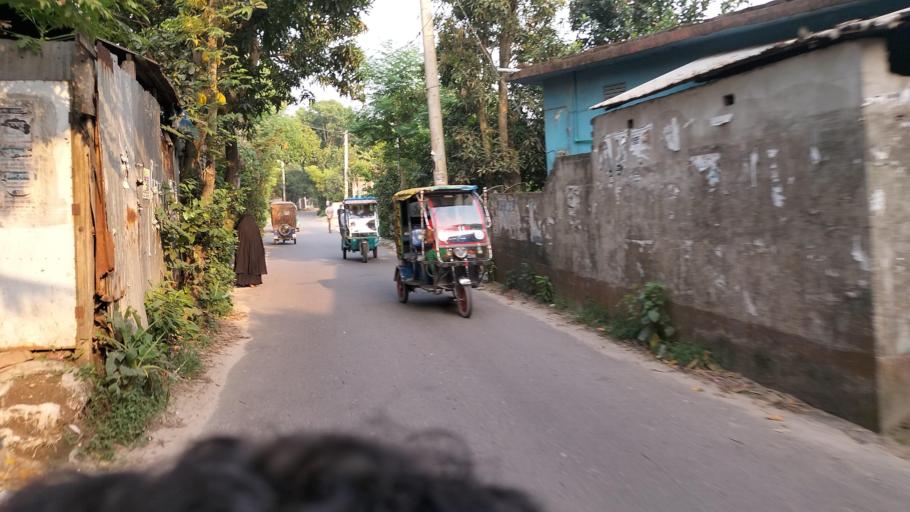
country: BD
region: Dhaka
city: Azimpur
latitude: 23.6661
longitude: 90.3282
